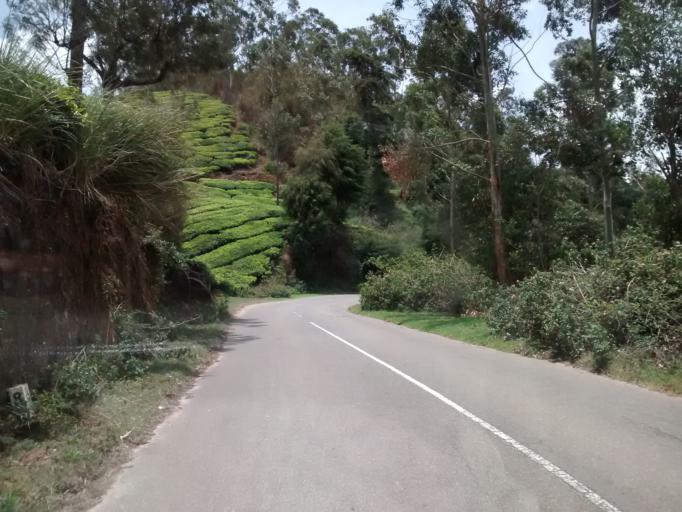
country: IN
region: Kerala
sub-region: Idukki
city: Munnar
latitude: 10.1298
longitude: 77.2120
